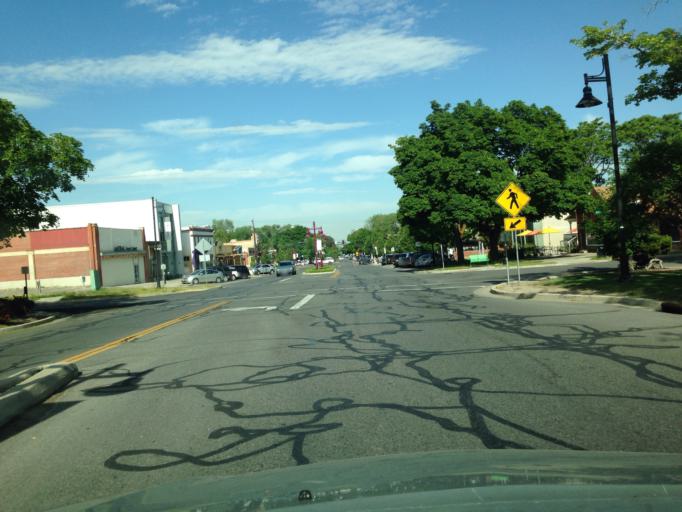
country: US
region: Utah
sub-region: Salt Lake County
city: Salt Lake City
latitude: 40.7498
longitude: -111.8635
